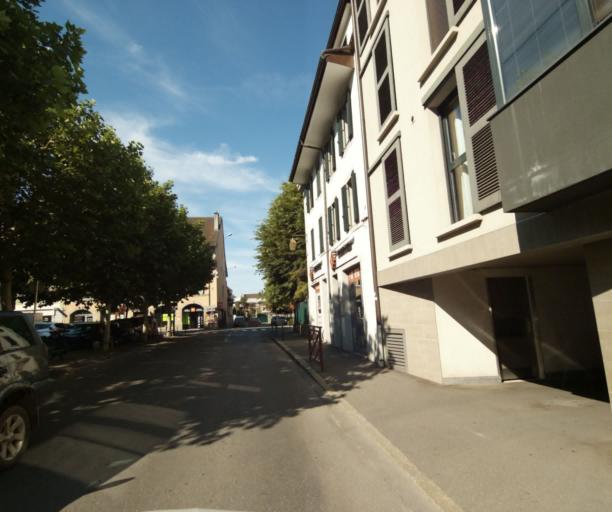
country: FR
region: Rhone-Alpes
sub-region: Departement de la Haute-Savoie
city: Thonon-les-Bains
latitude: 46.3726
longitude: 6.4774
